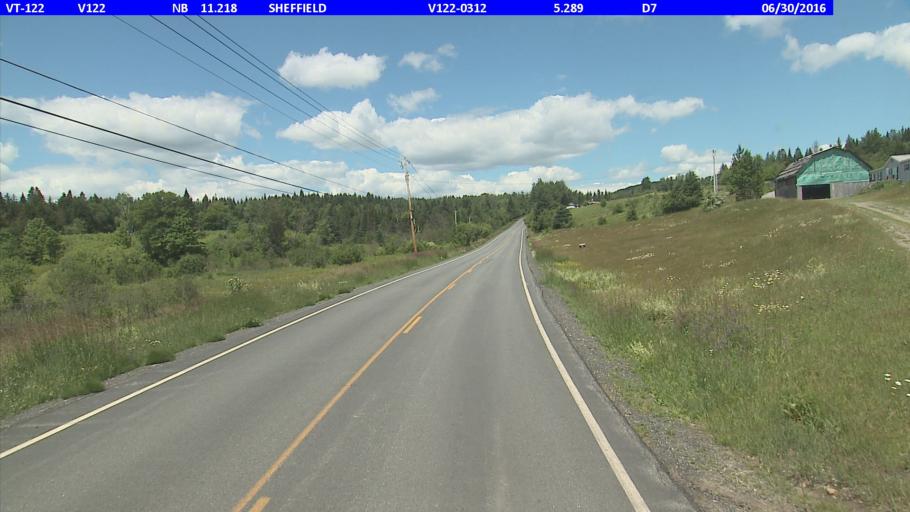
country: US
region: Vermont
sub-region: Caledonia County
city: Lyndonville
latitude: 44.6453
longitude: -72.1577
